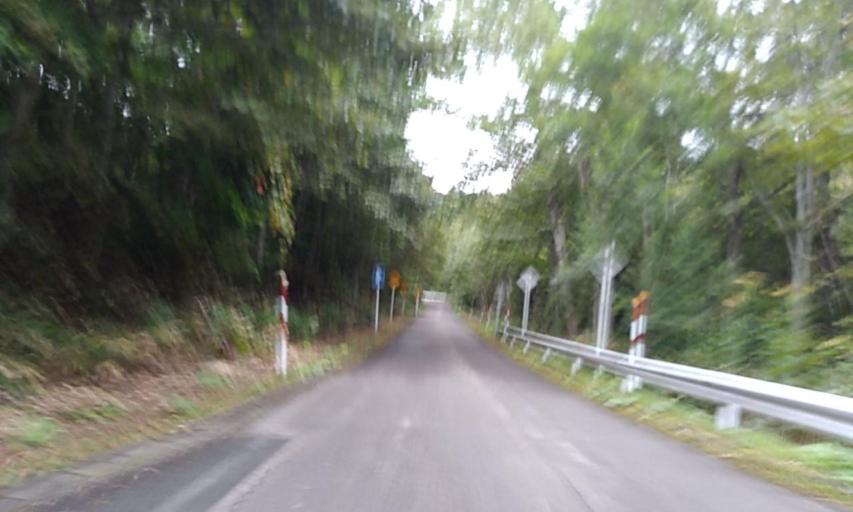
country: JP
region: Hokkaido
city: Bihoro
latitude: 43.5674
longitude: 144.1935
